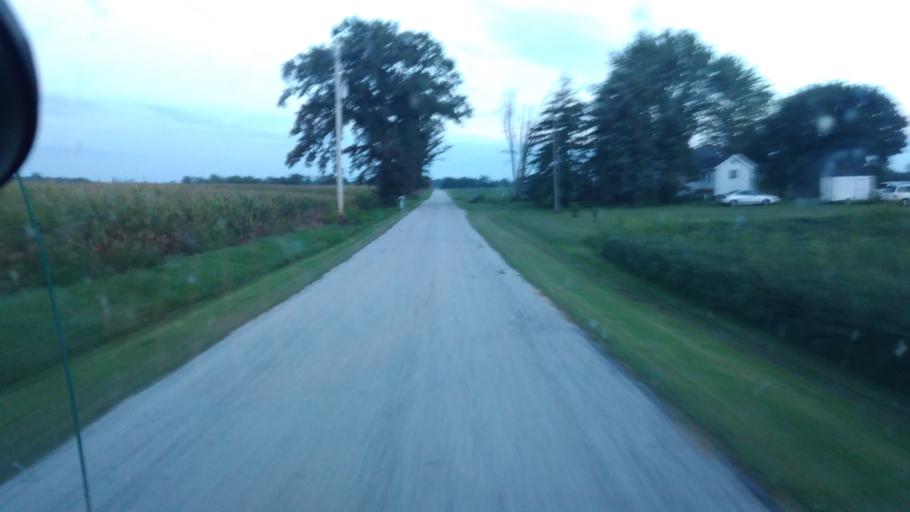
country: US
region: Ohio
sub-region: Hardin County
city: Forest
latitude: 40.6713
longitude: -83.4596
